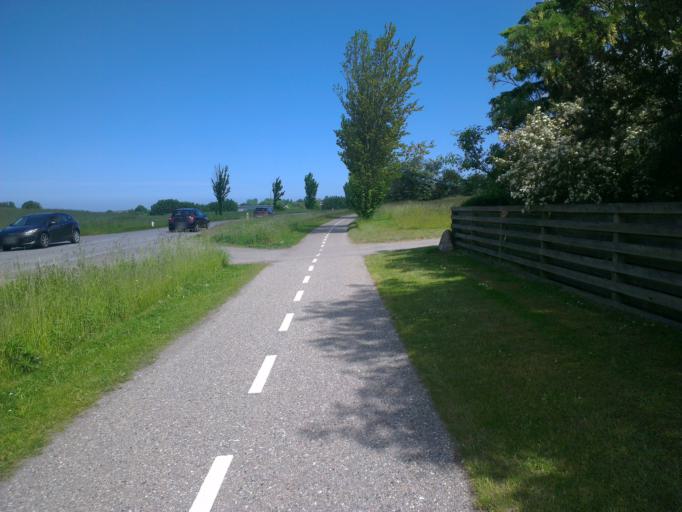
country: DK
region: Capital Region
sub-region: Frederikssund Kommune
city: Jaegerspris
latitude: 55.8295
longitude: 11.9882
